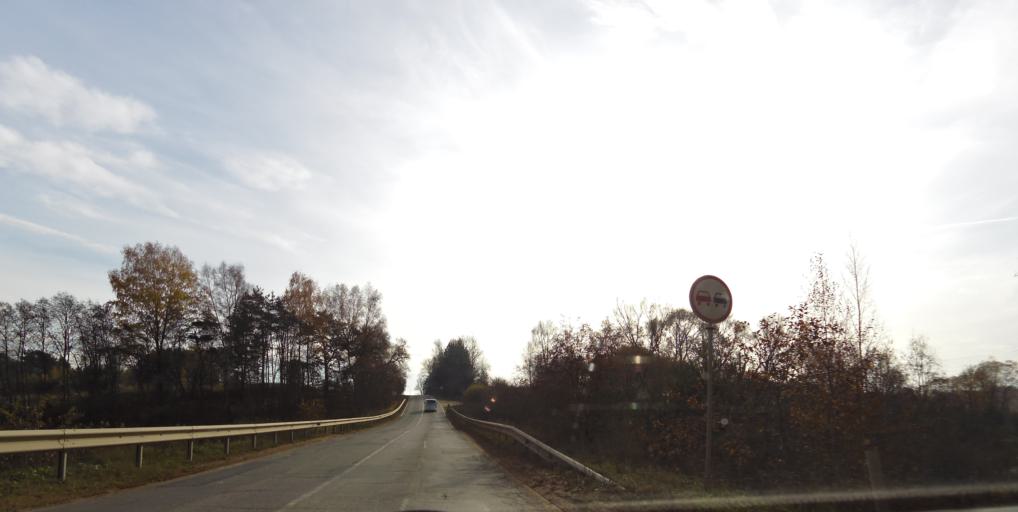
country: LT
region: Vilnius County
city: Justiniskes
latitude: 54.7128
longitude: 25.1992
